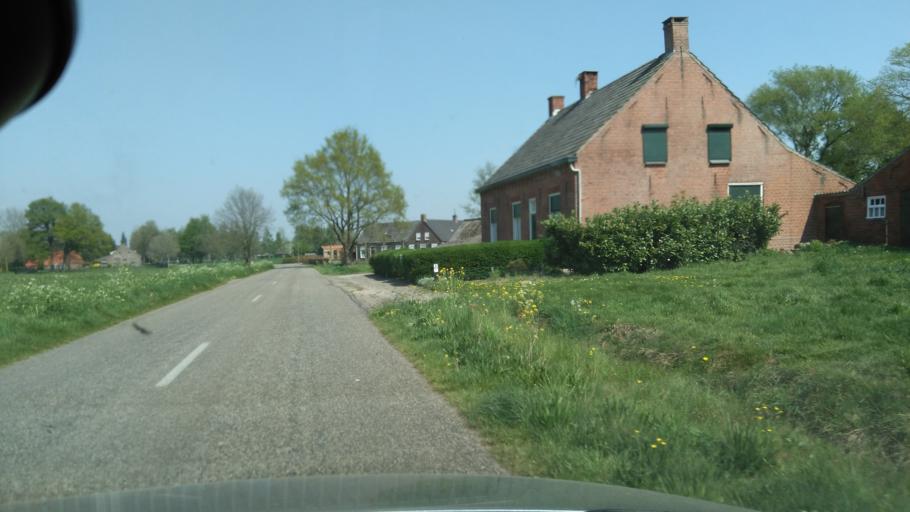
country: NL
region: North Brabant
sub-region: Gemeente Baarle-Nassau
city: Baarle-Nassau
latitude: 51.4645
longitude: 4.8703
